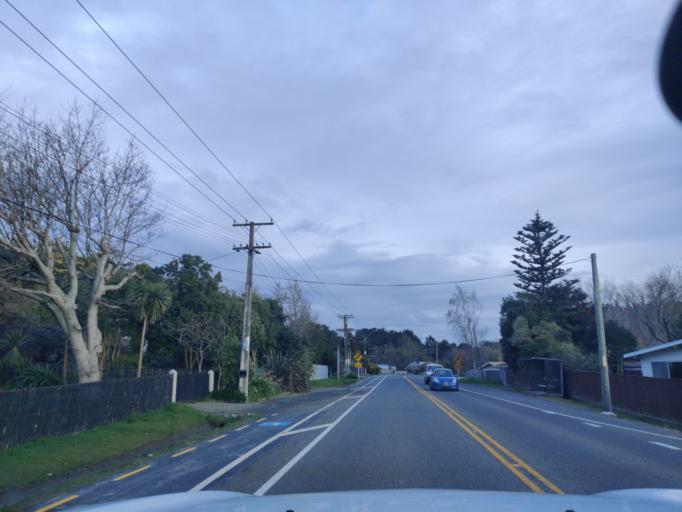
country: NZ
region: Manawatu-Wanganui
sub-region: Palmerston North City
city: Palmerston North
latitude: -40.3745
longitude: 175.6510
